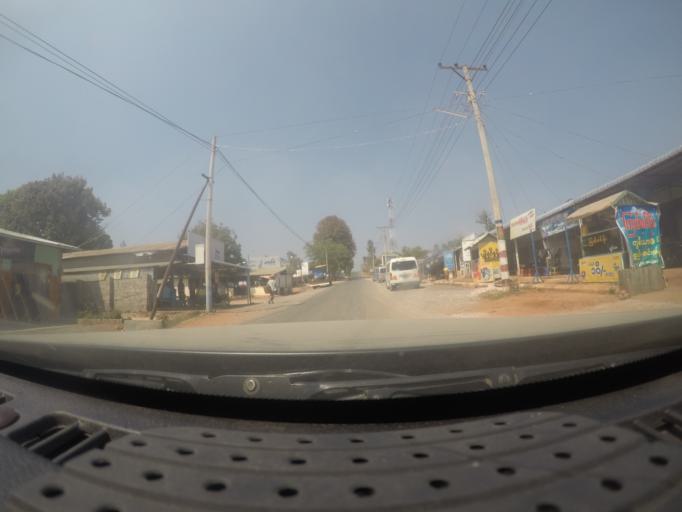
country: MM
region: Mandalay
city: Kyaukse
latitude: 21.1601
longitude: 96.4439
